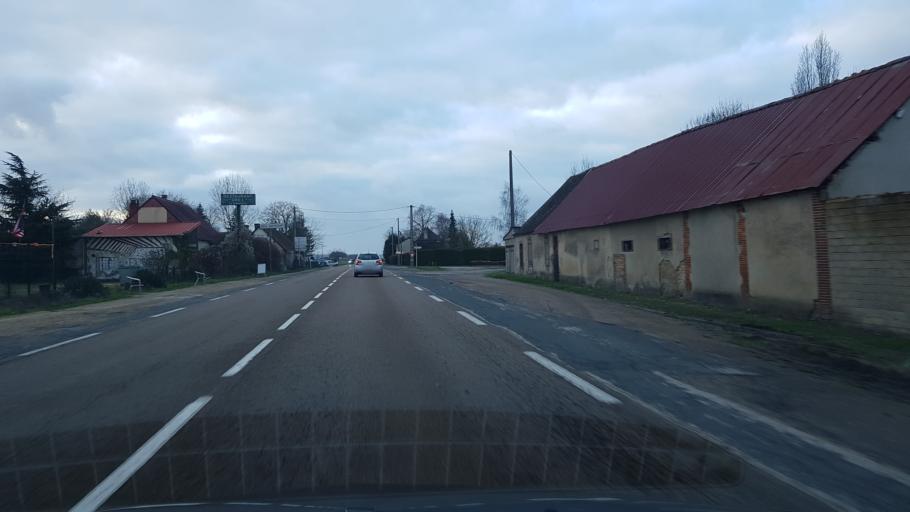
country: FR
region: Champagne-Ardenne
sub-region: Departement de la Marne
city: Connantre
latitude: 48.7252
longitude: 3.8407
